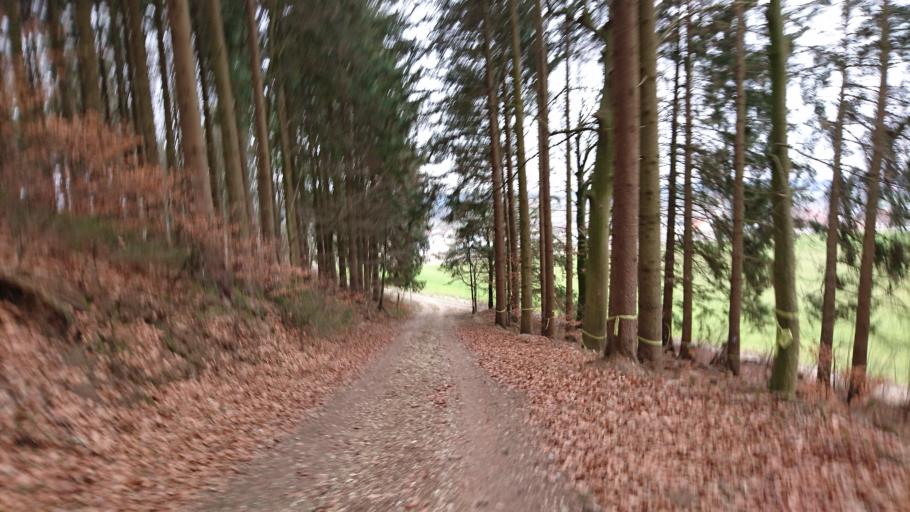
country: DE
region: Bavaria
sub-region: Swabia
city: Zusmarshausen
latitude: 48.4339
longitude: 10.6062
